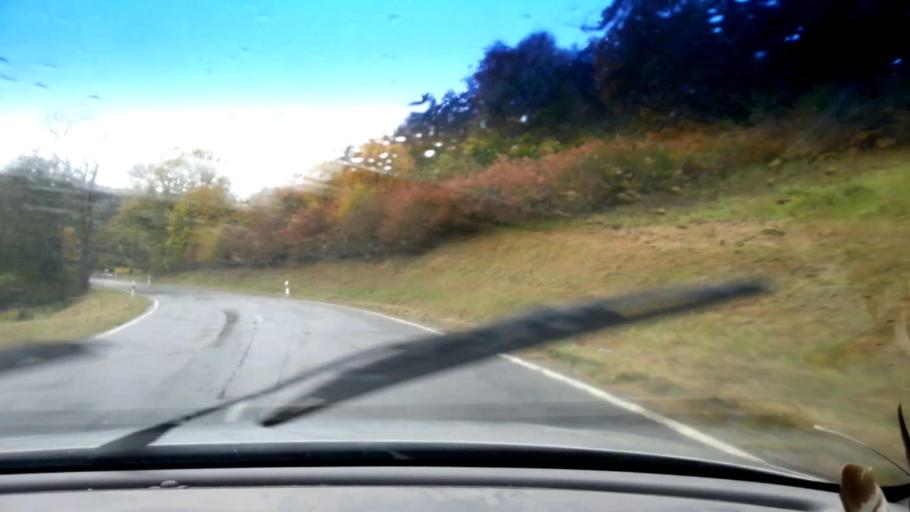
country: DE
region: Bavaria
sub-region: Upper Franconia
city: Heiligenstadt
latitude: 49.8913
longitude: 11.1610
